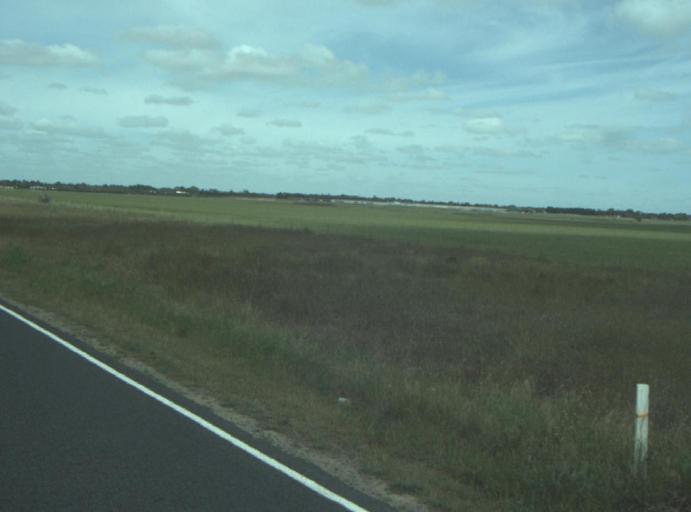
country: AU
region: Victoria
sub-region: Wyndham
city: Little River
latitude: -38.0071
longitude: 144.4634
